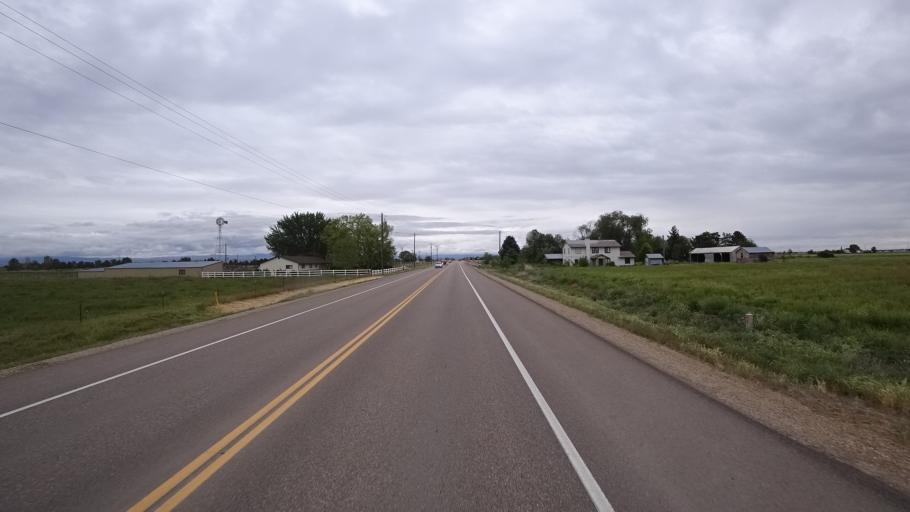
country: US
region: Idaho
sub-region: Ada County
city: Star
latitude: 43.6630
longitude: -116.4823
